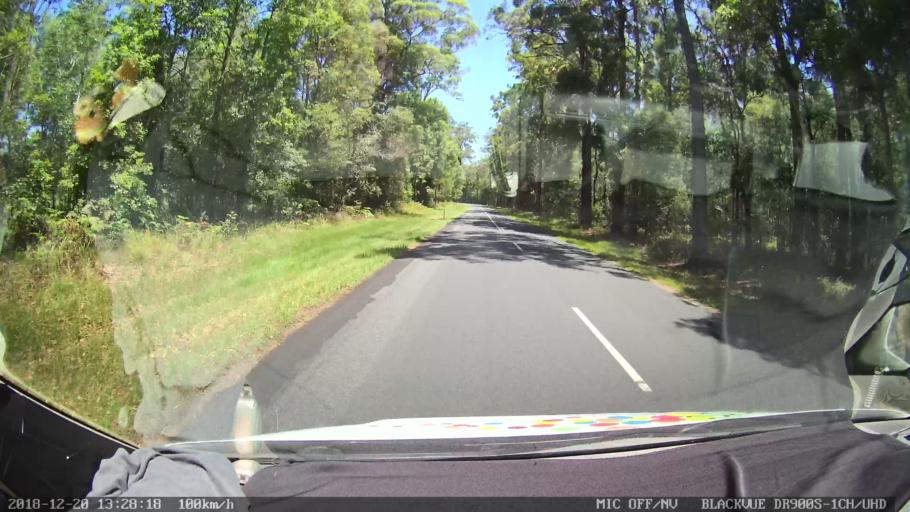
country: AU
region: New South Wales
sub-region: Clarence Valley
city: Gordon
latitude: -29.1726
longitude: 152.9909
